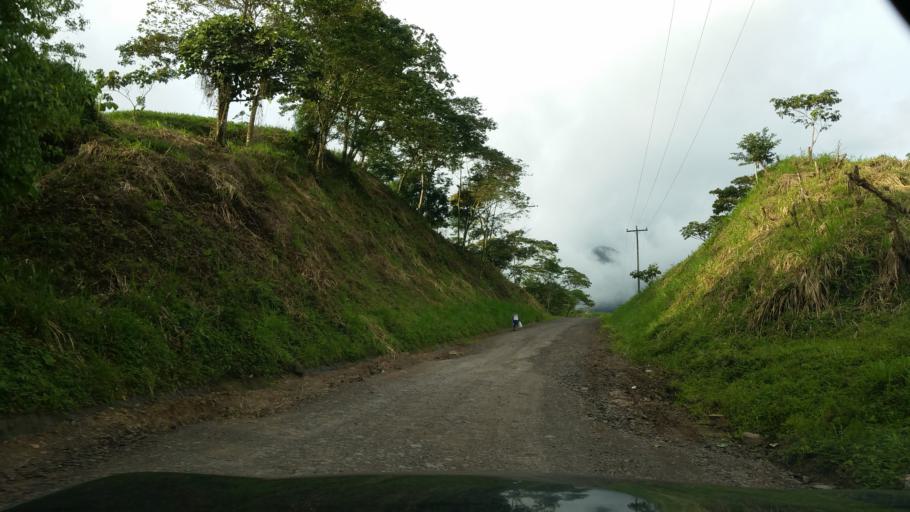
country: NI
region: Jinotega
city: Jinotega
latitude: 13.2645
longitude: -85.7324
